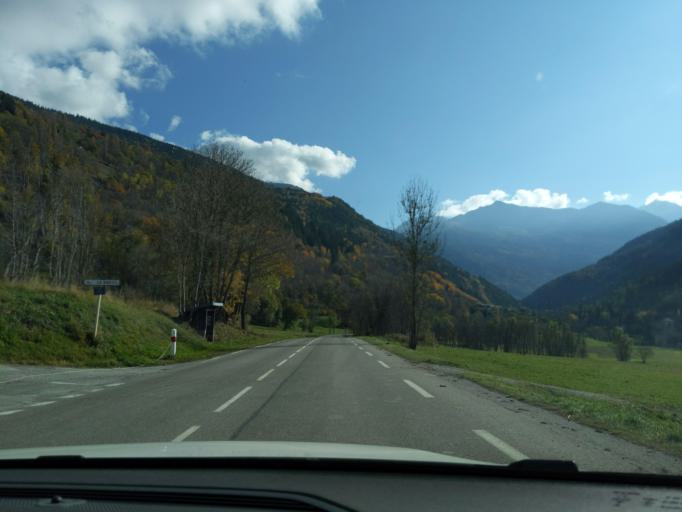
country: FR
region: Rhone-Alpes
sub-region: Departement de la Savoie
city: Seez
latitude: 45.6173
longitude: 6.8128
